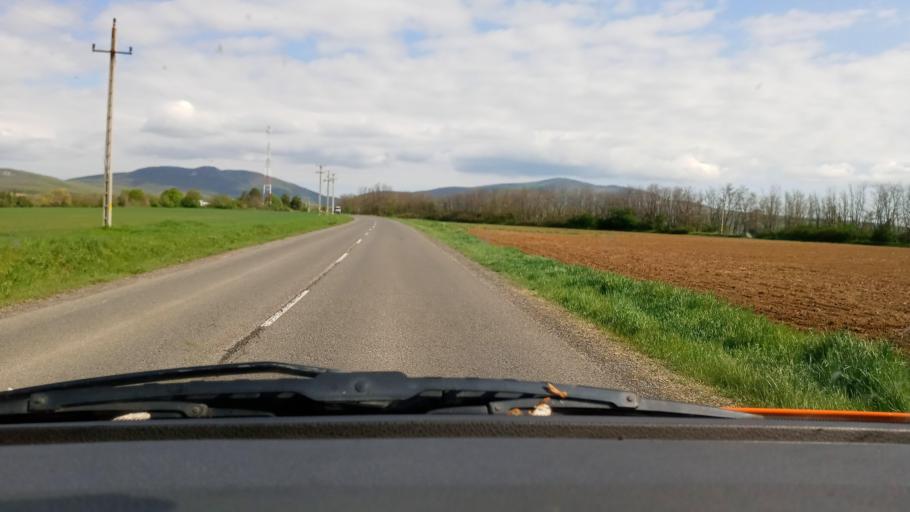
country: HU
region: Baranya
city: Hosszuheteny
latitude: 46.1214
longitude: 18.3485
